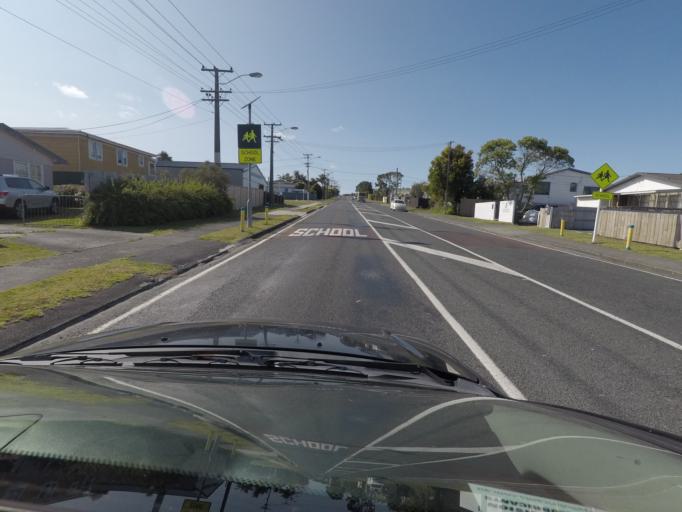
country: NZ
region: Auckland
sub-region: Auckland
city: Warkworth
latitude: -36.4239
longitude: 174.7273
